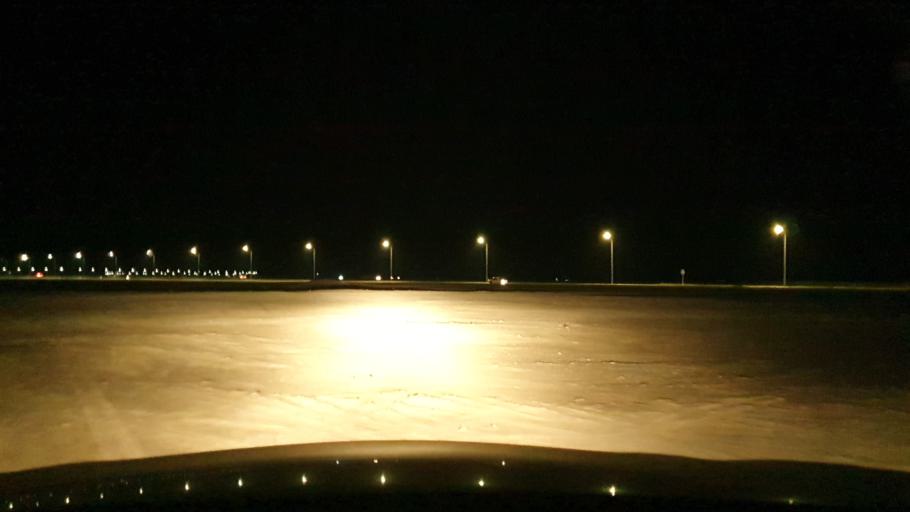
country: BH
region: Muharraq
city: Al Muharraq
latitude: 26.2812
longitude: 50.5861
